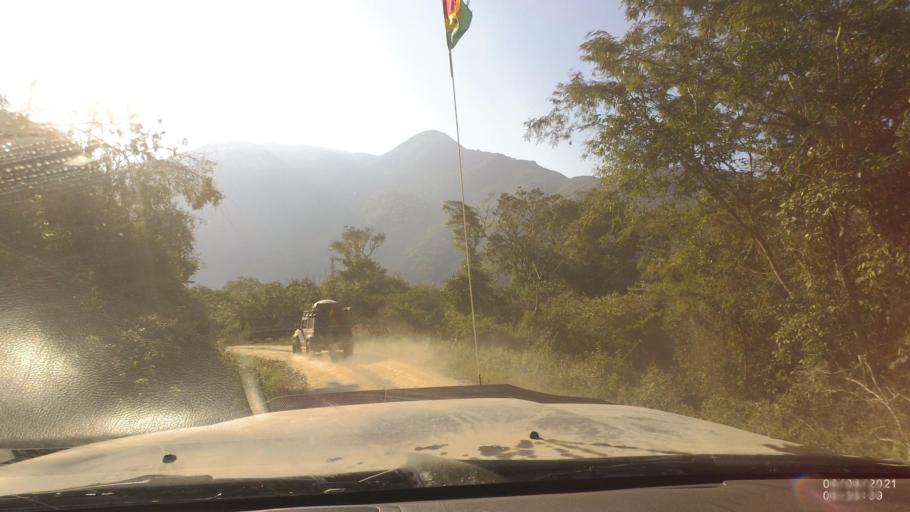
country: BO
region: La Paz
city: Quime
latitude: -16.5289
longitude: -66.7642
